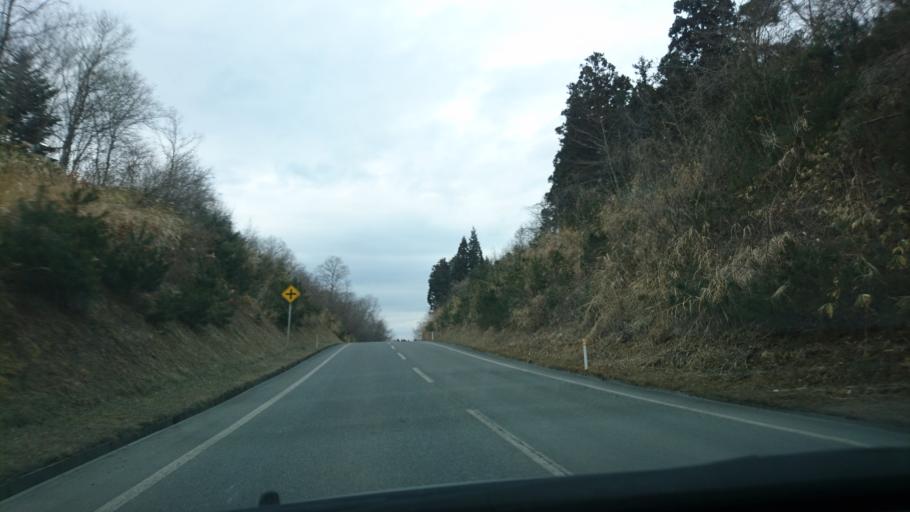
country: JP
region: Iwate
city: Ichinoseki
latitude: 38.9745
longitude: 141.3557
